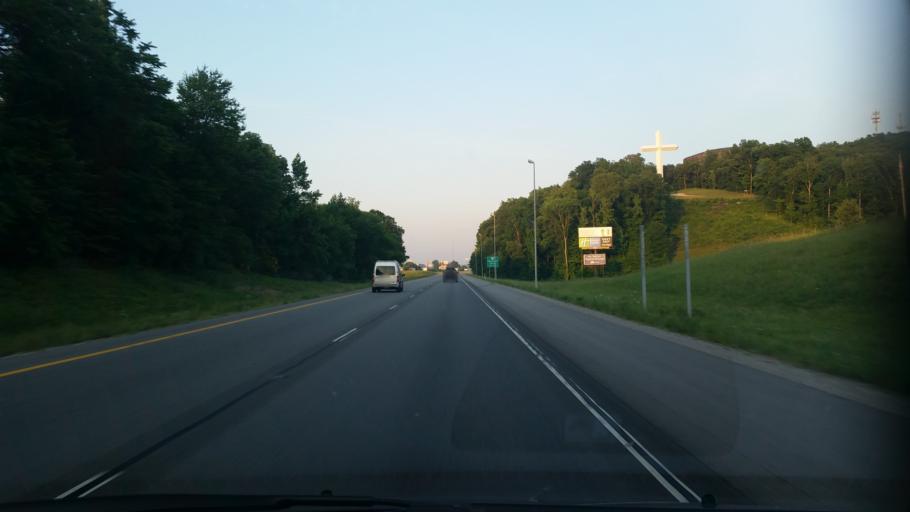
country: US
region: Tennessee
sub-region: Putnam County
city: Cookeville
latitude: 36.1362
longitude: -85.5213
